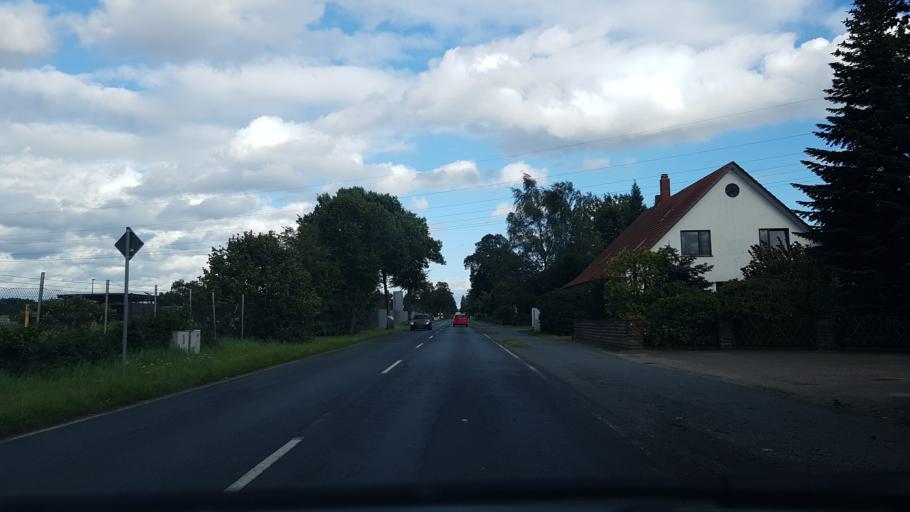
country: DE
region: Lower Saxony
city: Achim
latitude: 53.0230
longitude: 8.9888
